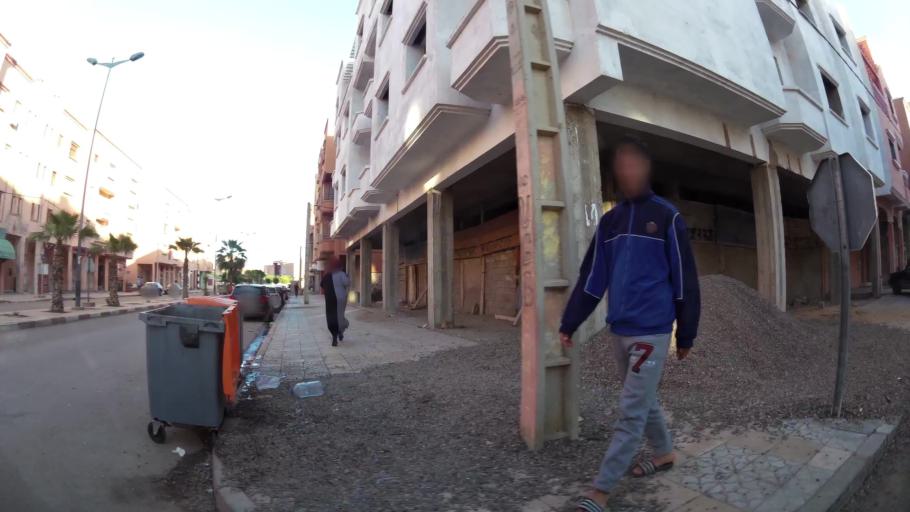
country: MA
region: Marrakech-Tensift-Al Haouz
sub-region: Kelaa-Des-Sraghna
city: Sidi Abdallah
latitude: 32.2403
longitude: -7.9615
